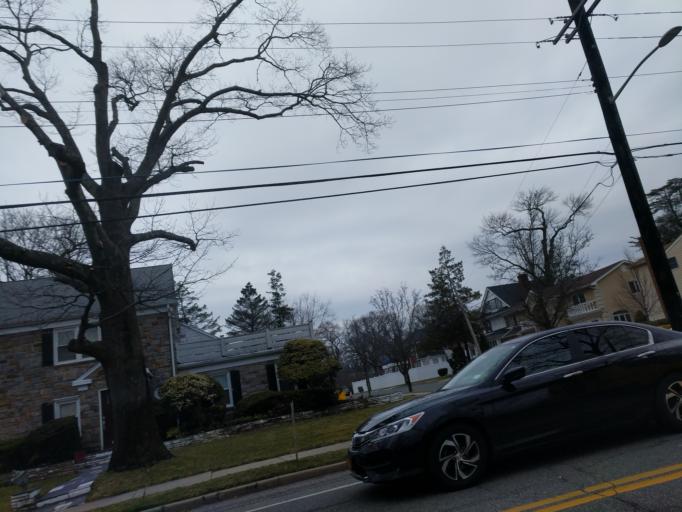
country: US
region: New York
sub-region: Nassau County
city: Woodmere
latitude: 40.6261
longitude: -73.7159
